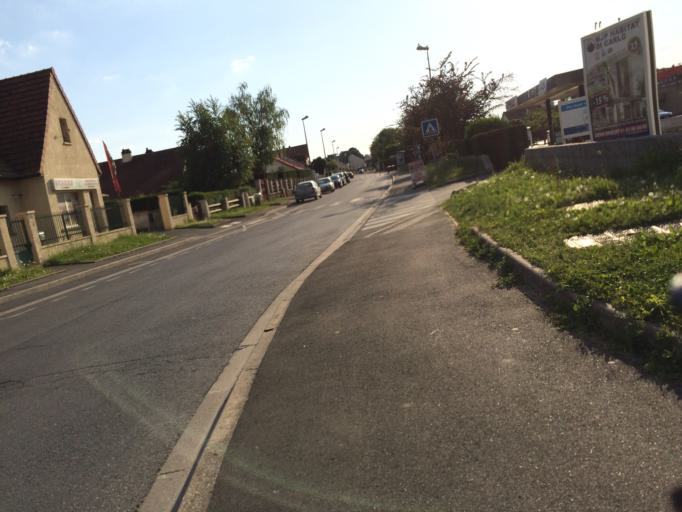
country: FR
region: Ile-de-France
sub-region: Departement de l'Essonne
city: Lisses
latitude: 48.5998
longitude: 2.4350
